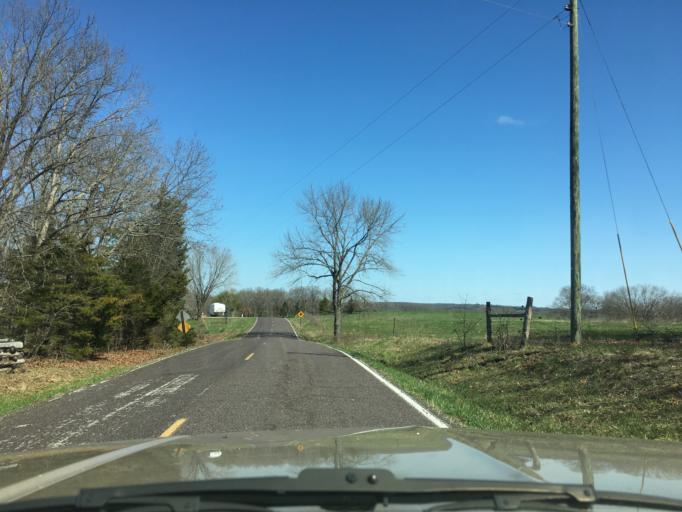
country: US
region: Missouri
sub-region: Franklin County
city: New Haven
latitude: 38.5382
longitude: -91.3288
